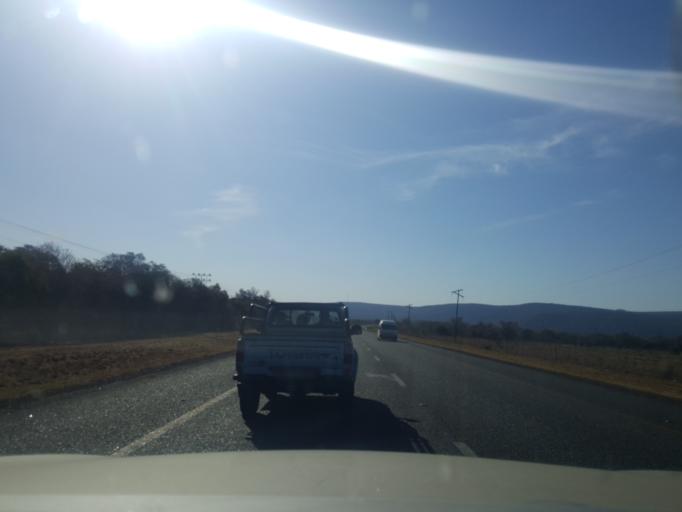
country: ZA
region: North-West
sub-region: Ngaka Modiri Molema District Municipality
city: Zeerust
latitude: -25.5363
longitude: 26.1940
